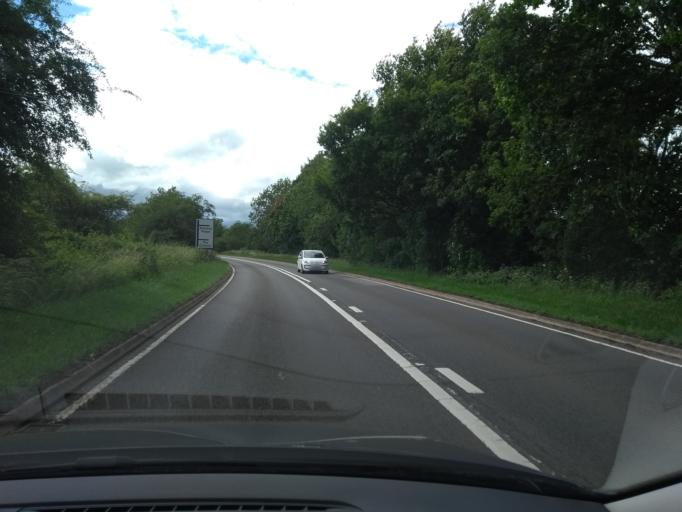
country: GB
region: England
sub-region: Warwickshire
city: Henley in Arden
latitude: 52.2864
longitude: -1.7433
